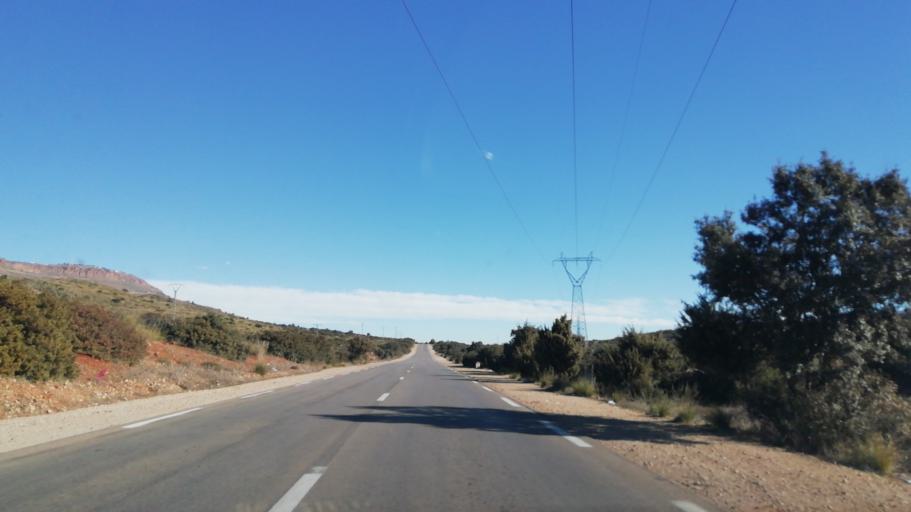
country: DZ
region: Tlemcen
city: Sebdou
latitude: 34.7157
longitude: -1.2054
